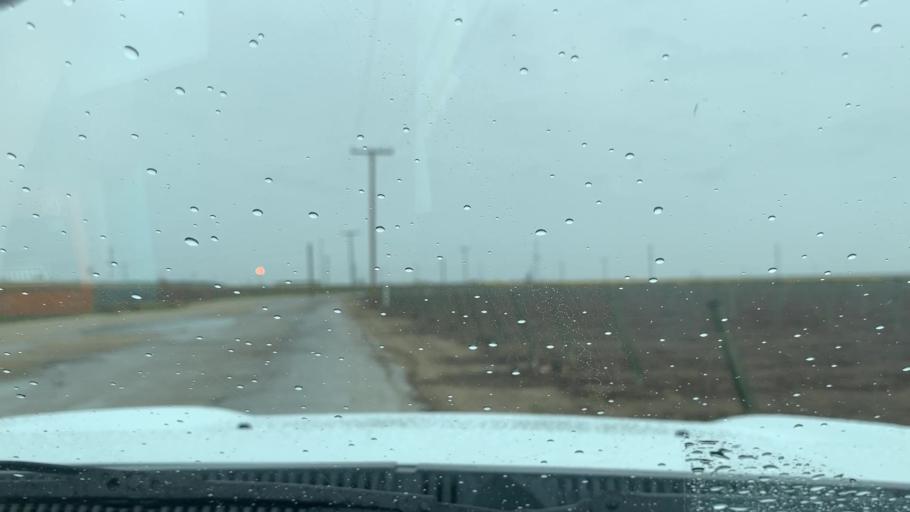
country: US
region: California
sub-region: Tulare County
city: Richgrove
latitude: 35.8375
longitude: -119.1621
